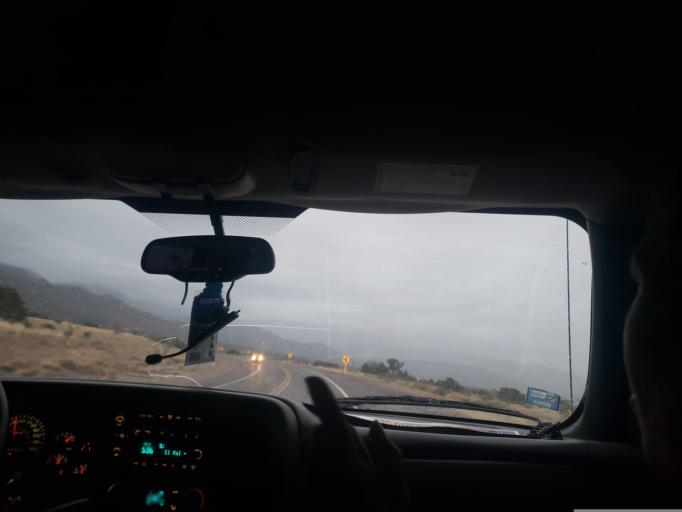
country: US
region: New Mexico
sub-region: Bernalillo County
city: Sandia Heights
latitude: 35.1963
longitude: -106.5022
